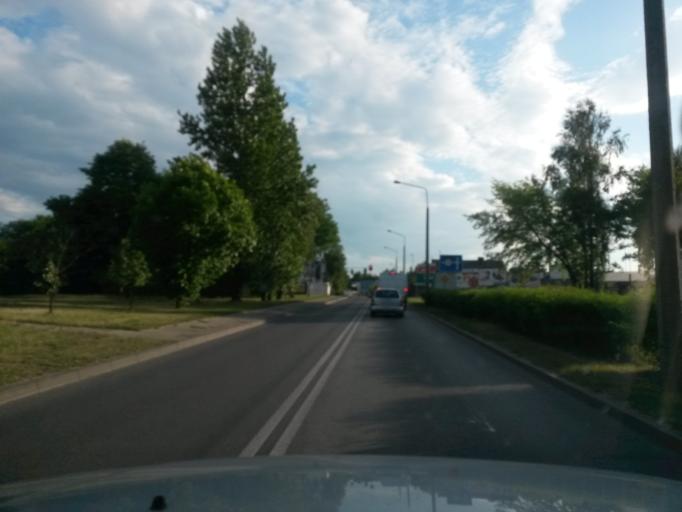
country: PL
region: Lodz Voivodeship
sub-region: Powiat belchatowski
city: Belchatow
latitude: 51.3696
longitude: 19.3577
